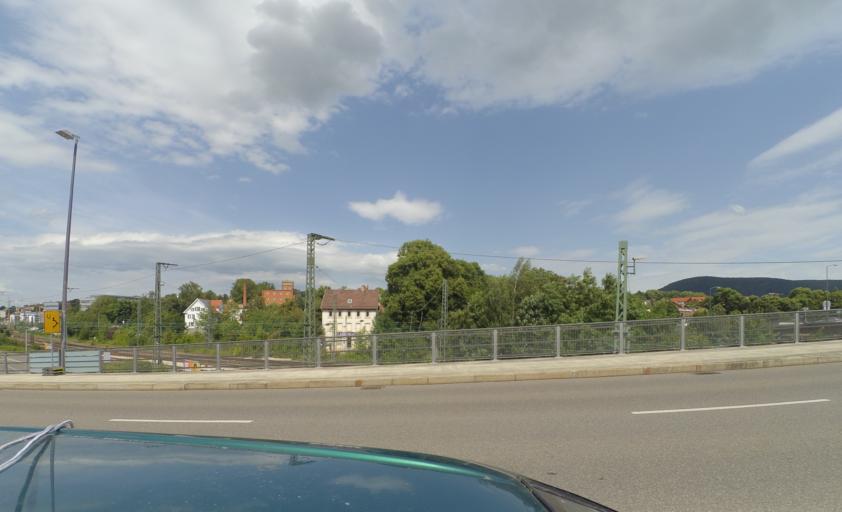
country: DE
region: Baden-Wuerttemberg
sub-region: Regierungsbezirk Stuttgart
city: Aalen
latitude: 48.8374
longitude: 10.0964
